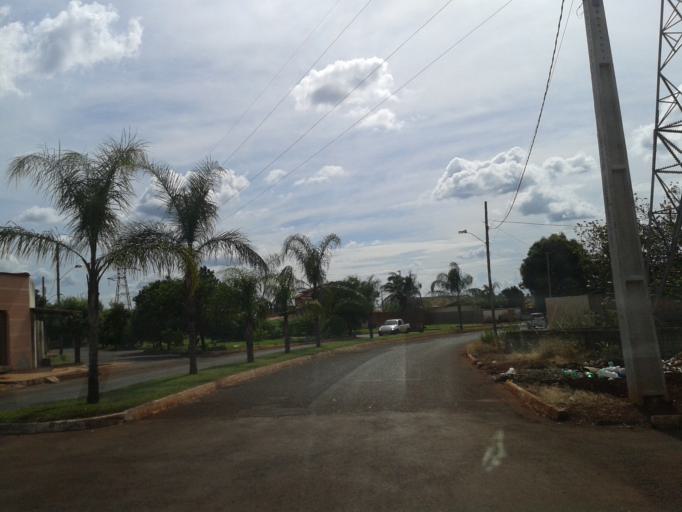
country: BR
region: Minas Gerais
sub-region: Centralina
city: Centralina
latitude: -18.5928
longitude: -49.1984
